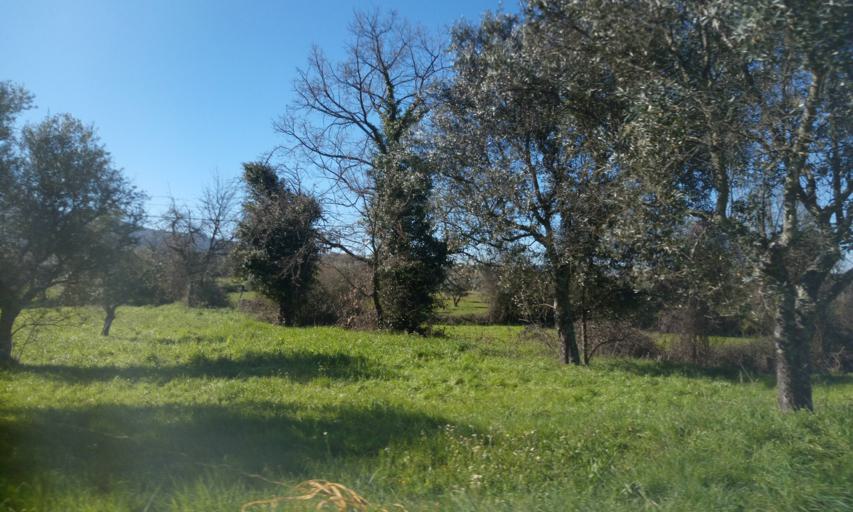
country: PT
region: Guarda
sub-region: Fornos de Algodres
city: Fornos de Algodres
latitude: 40.5289
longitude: -7.5575
